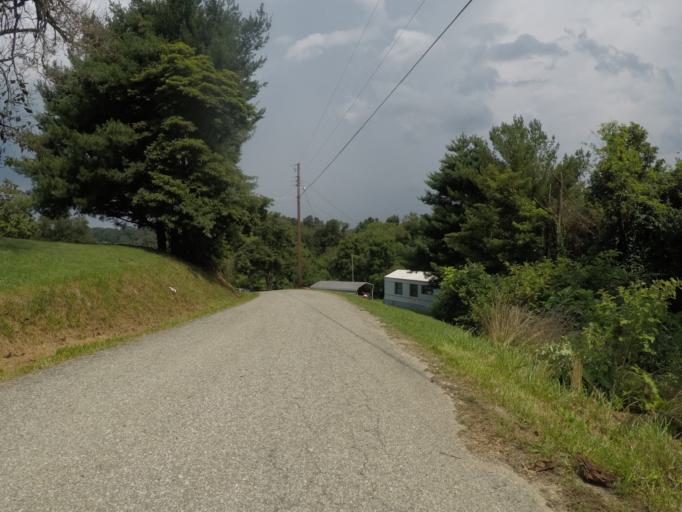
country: US
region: Kentucky
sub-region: Boyd County
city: Ironville
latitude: 38.4438
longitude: -82.7070
